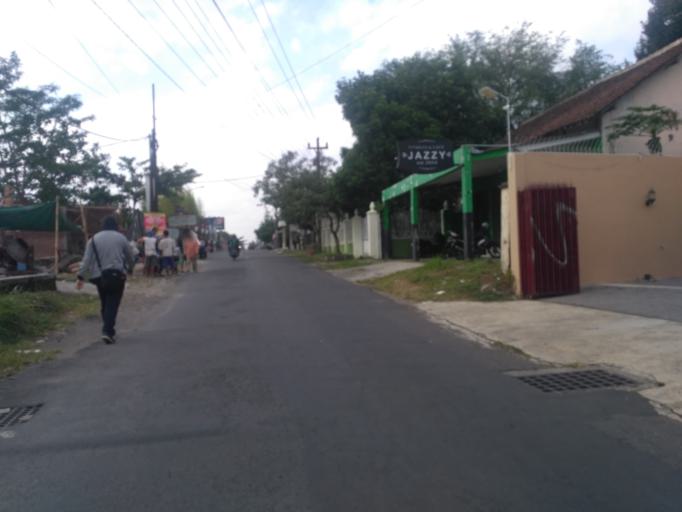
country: ID
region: Daerah Istimewa Yogyakarta
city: Yogyakarta
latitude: -7.7669
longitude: 110.3531
